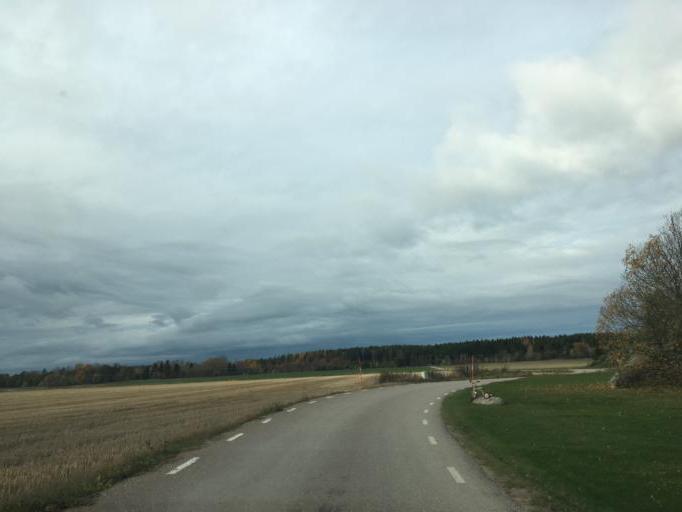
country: SE
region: Vaestmanland
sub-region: Hallstahammars Kommun
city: Kolback
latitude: 59.5492
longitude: 16.3444
